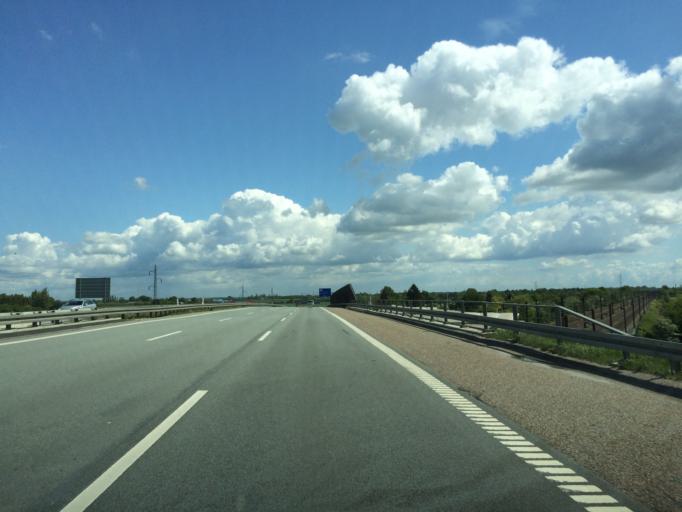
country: DK
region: Zealand
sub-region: Roskilde Kommune
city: Vindinge
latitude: 55.6480
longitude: 12.1415
